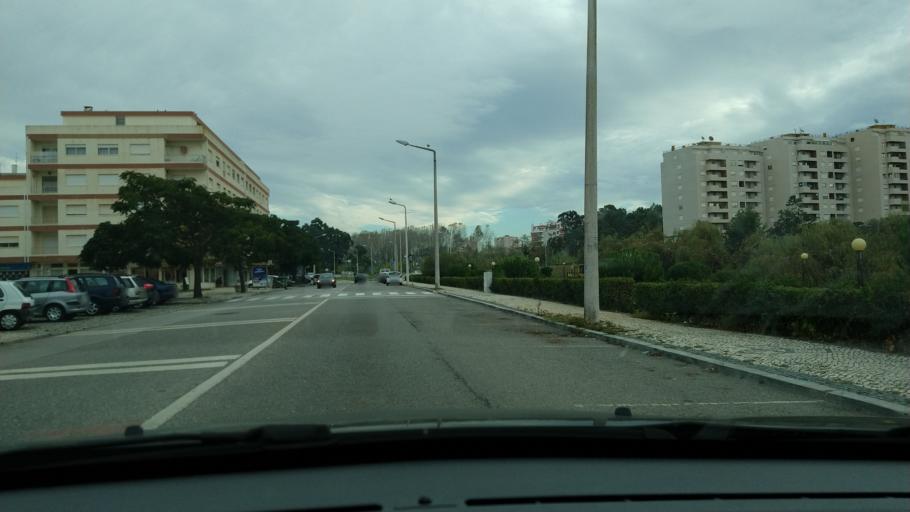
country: PT
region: Coimbra
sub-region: Figueira da Foz
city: Figueira da Foz
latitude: 40.1588
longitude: -8.8594
